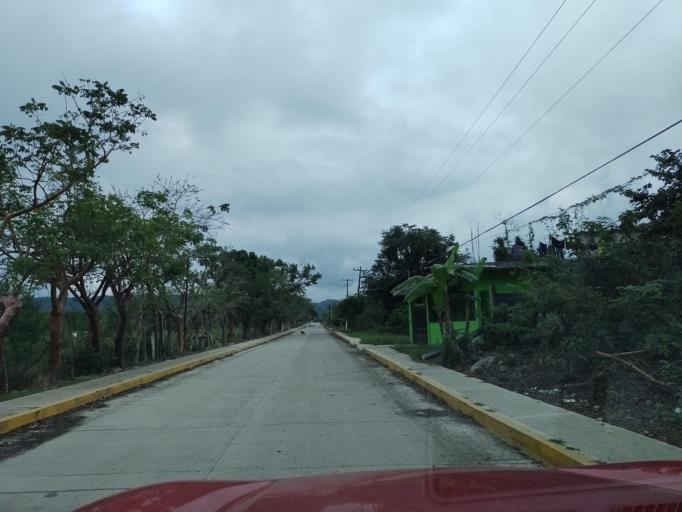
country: MX
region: Veracruz
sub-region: Papantla
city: El Chote
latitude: 20.4318
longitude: -97.3809
